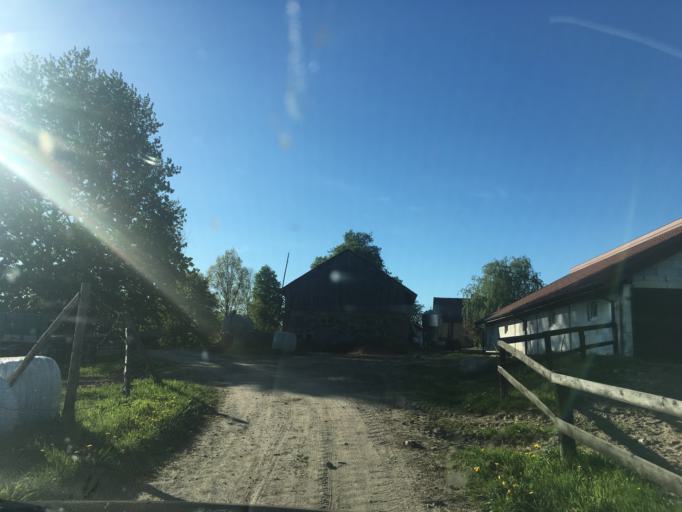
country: PL
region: Warmian-Masurian Voivodeship
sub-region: Powiat piski
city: Ruciane-Nida
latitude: 53.6623
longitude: 21.4774
